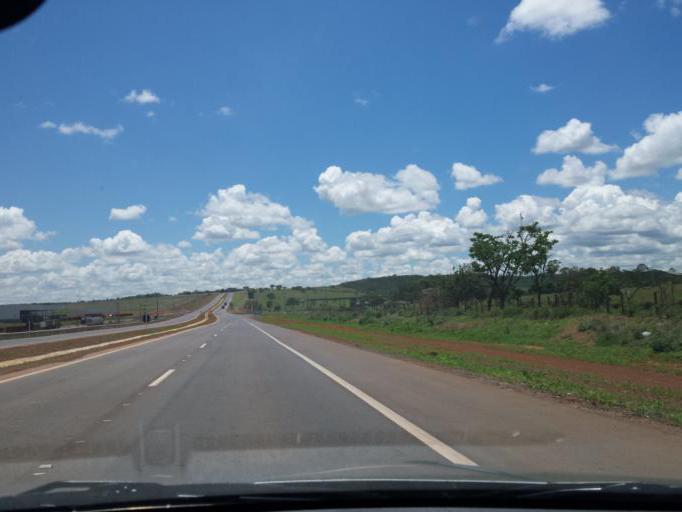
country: BR
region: Goias
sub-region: Cristalina
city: Cristalina
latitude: -16.6192
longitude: -47.7519
